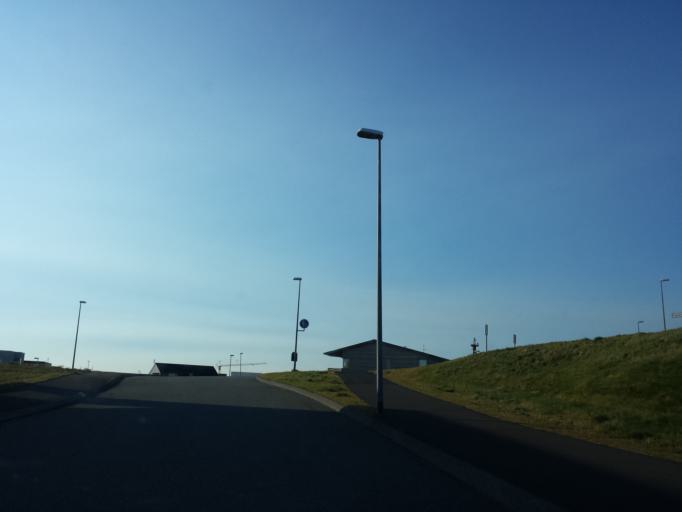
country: IS
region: Capital Region
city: Reykjavik
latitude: 64.0859
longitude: -21.8151
